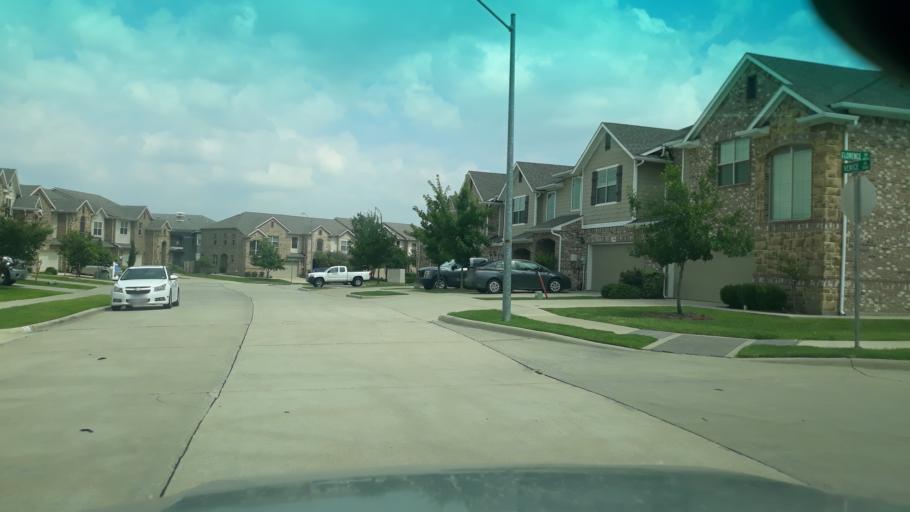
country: US
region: Texas
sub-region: Dallas County
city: Irving
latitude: 32.8673
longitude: -96.9975
